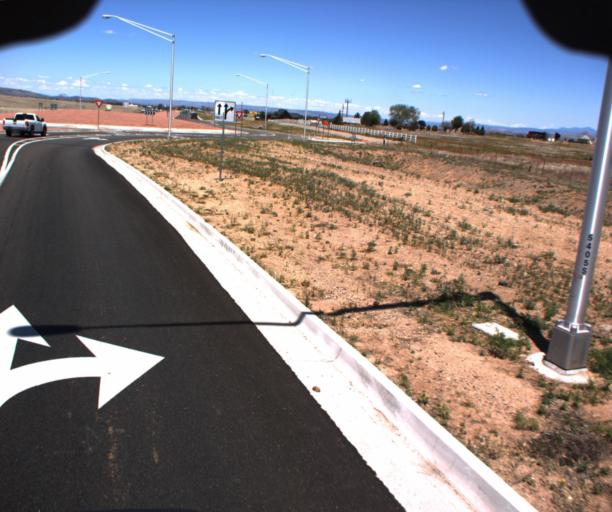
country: US
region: Arizona
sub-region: Yavapai County
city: Chino Valley
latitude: 34.7043
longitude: -112.4501
